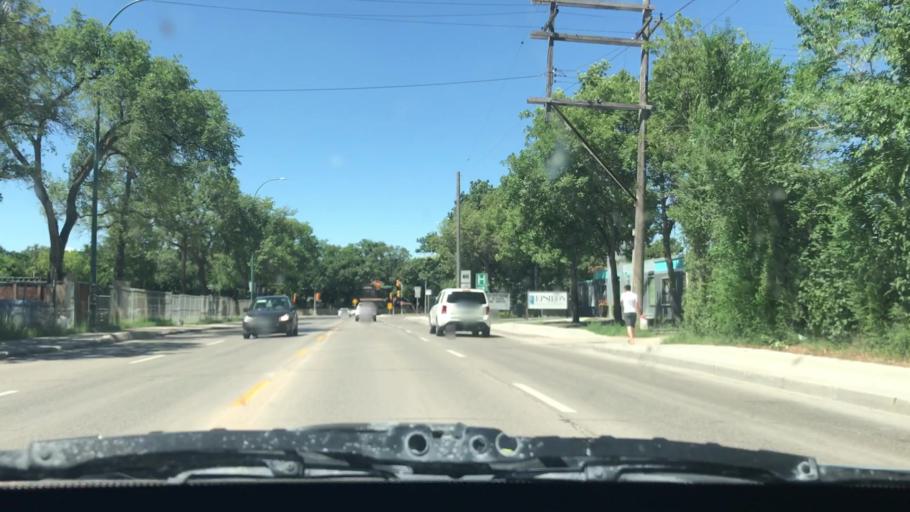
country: CA
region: Manitoba
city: Winnipeg
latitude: 49.8737
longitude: -97.1660
